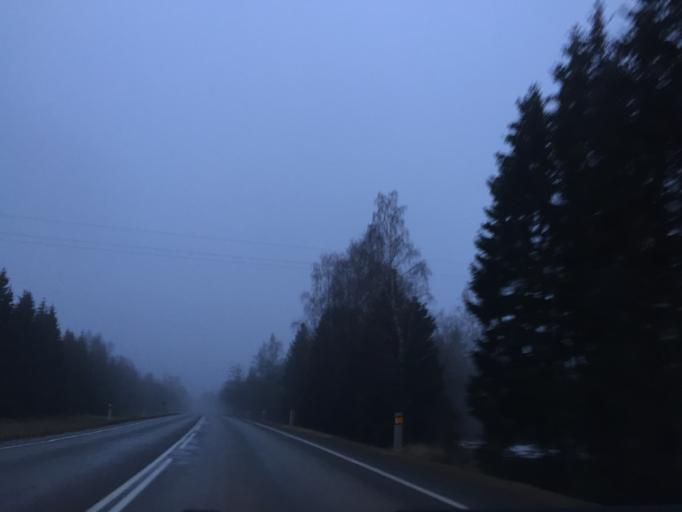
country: EE
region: Laeaene
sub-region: Lihula vald
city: Lihula
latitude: 58.6362
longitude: 23.6891
